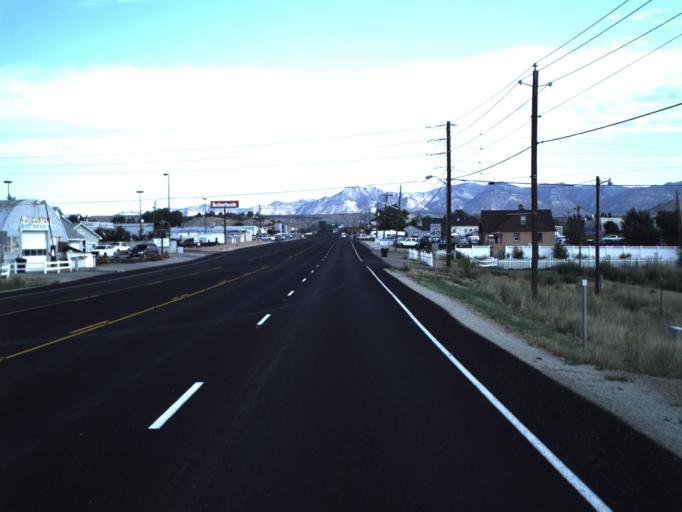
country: US
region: Utah
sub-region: Carbon County
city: Price
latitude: 39.5912
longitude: -110.7897
